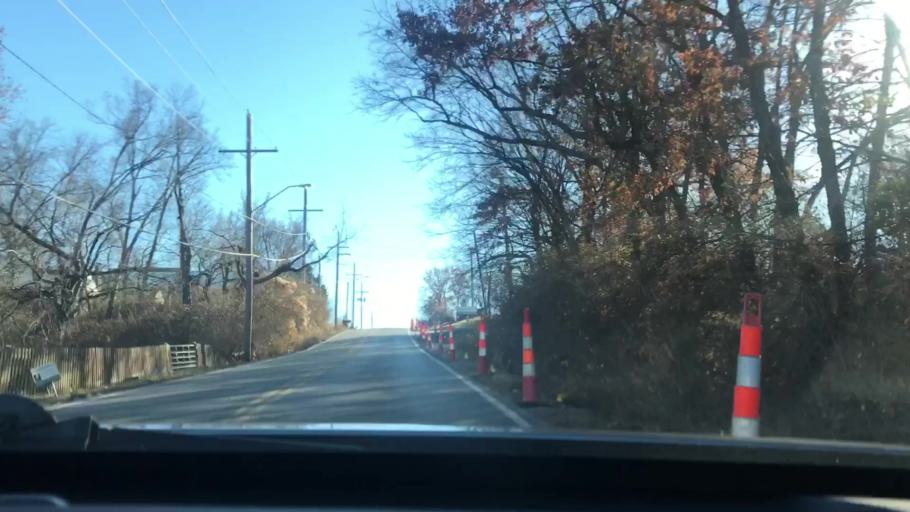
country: US
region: Missouri
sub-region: Jackson County
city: Raytown
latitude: 38.9718
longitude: -94.5209
